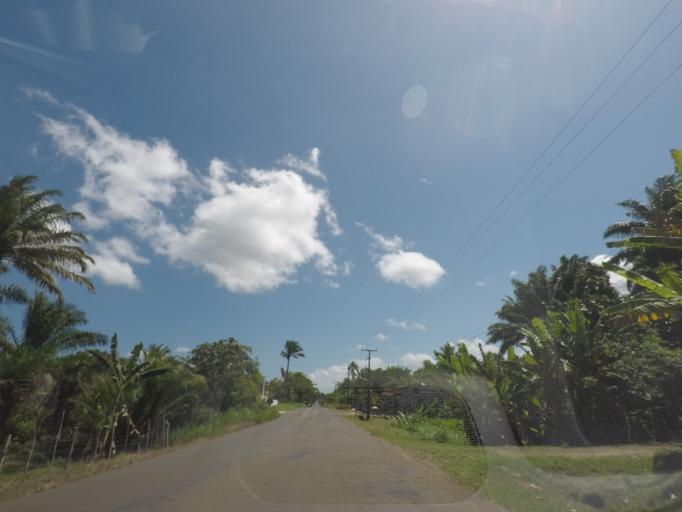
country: BR
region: Bahia
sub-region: Valenca
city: Valenca
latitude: -13.3919
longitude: -39.0756
